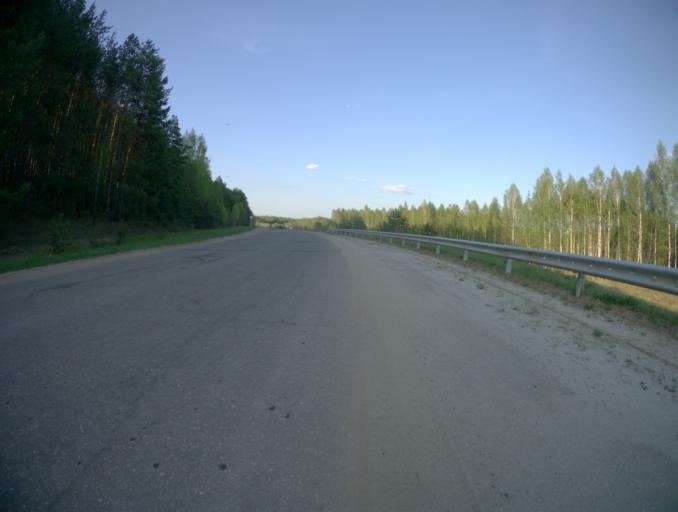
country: RU
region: Ivanovo
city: Yuzha
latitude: 56.5801
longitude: 41.9203
